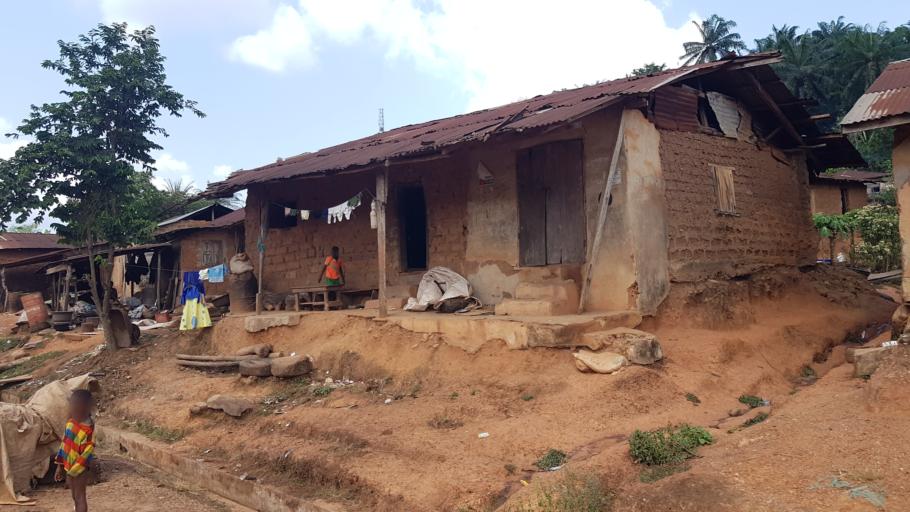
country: NG
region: Osun
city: Ifetedo
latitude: 7.0173
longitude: 4.6327
